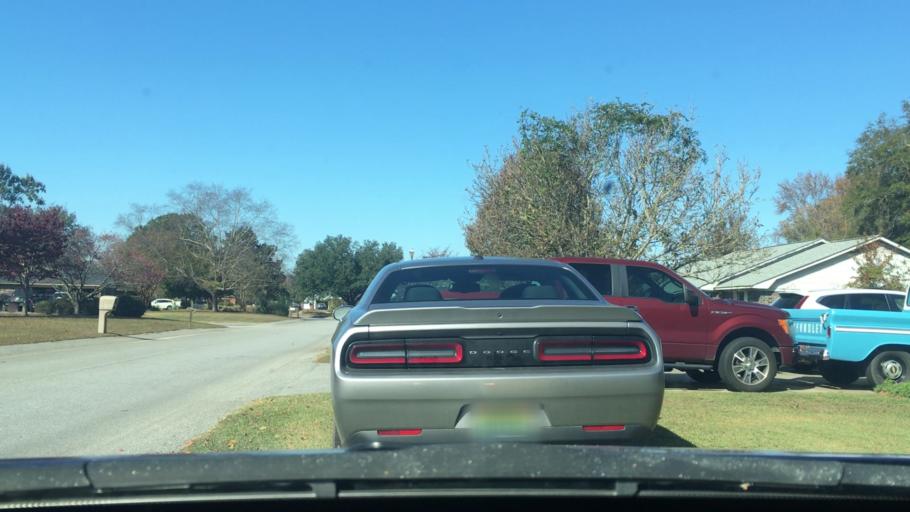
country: US
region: South Carolina
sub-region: Sumter County
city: Cane Savannah
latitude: 33.9141
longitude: -80.4115
